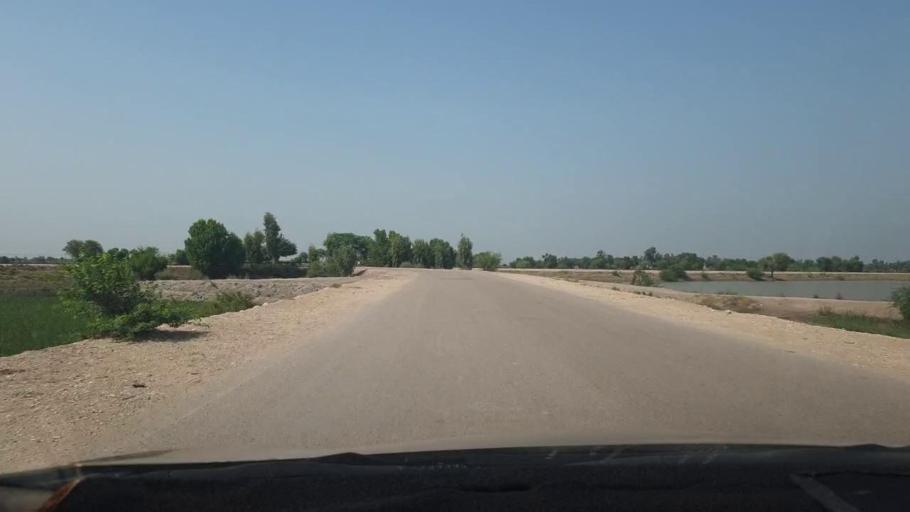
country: PK
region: Sindh
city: Larkana
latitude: 27.5969
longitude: 68.2436
